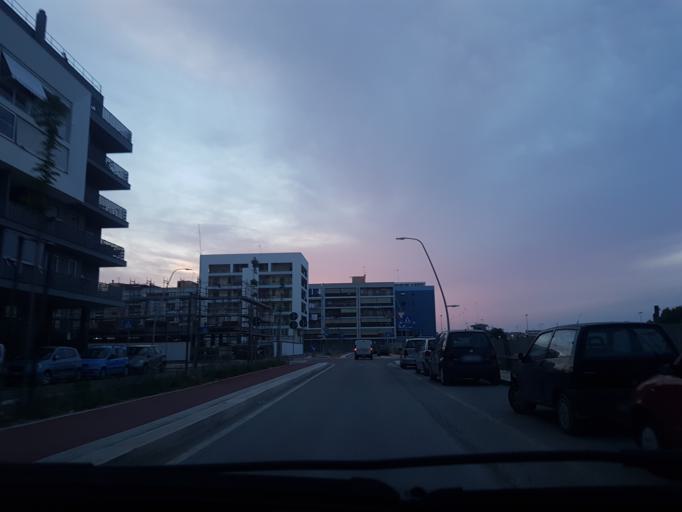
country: IT
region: Apulia
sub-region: Provincia di Barletta - Andria - Trani
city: Barletta
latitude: 41.3060
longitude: 16.2667
